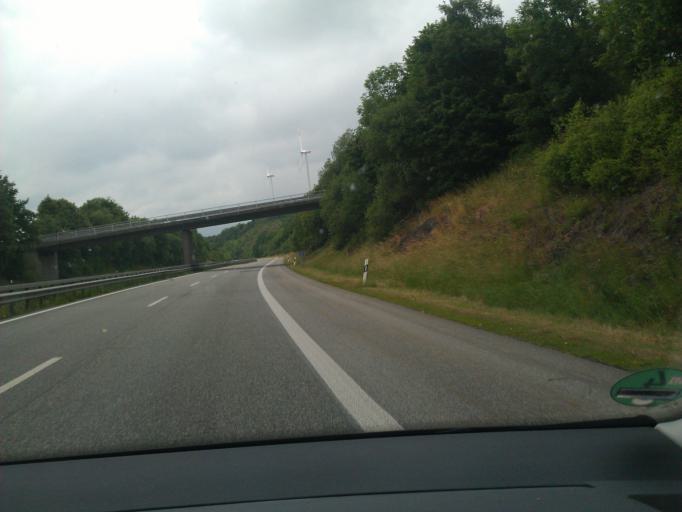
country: DE
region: Rheinland-Pfalz
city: Leitzweiler
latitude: 49.5811
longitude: 7.2165
